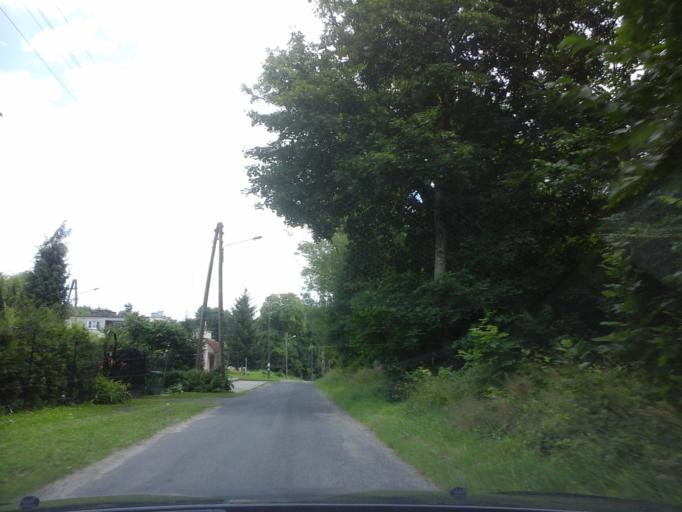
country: PL
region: West Pomeranian Voivodeship
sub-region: Powiat choszczenski
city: Recz
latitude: 53.2910
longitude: 15.5418
